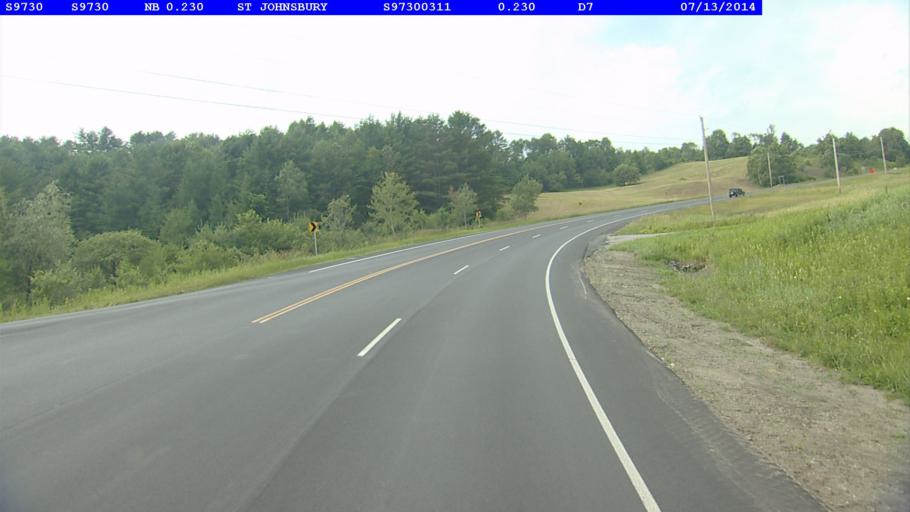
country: US
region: Vermont
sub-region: Caledonia County
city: St Johnsbury
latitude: 44.4455
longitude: -72.0202
